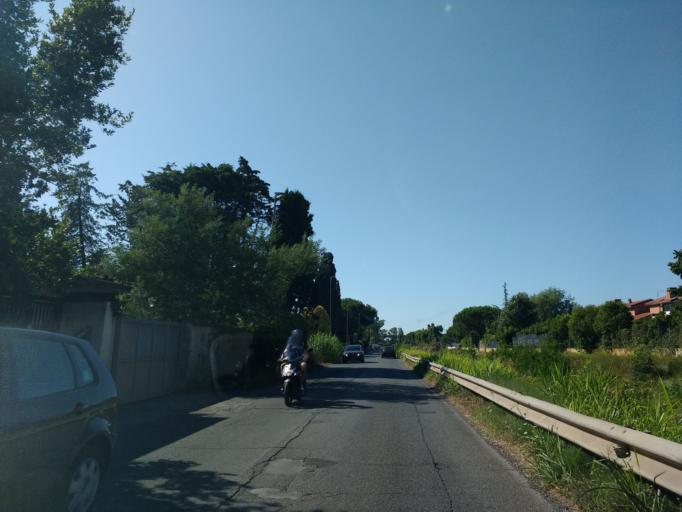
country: IT
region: Latium
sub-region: Citta metropolitana di Roma Capitale
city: Acilia-Castel Fusano-Ostia Antica
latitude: 41.7464
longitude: 12.3345
